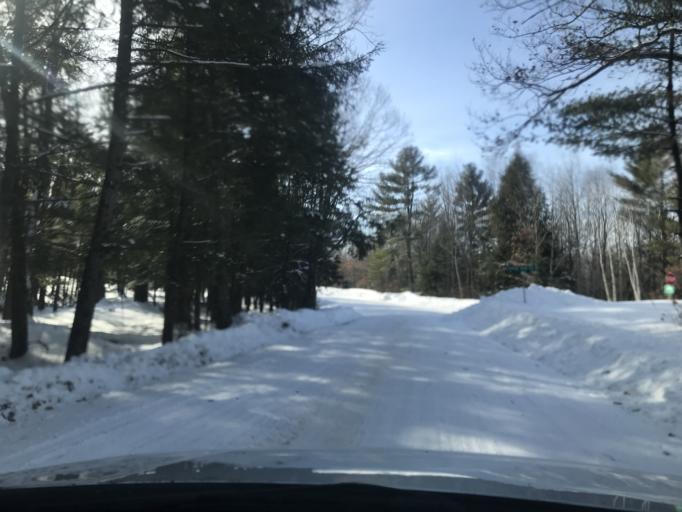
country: US
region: Wisconsin
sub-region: Oconto County
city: Gillett
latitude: 45.1495
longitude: -88.2395
